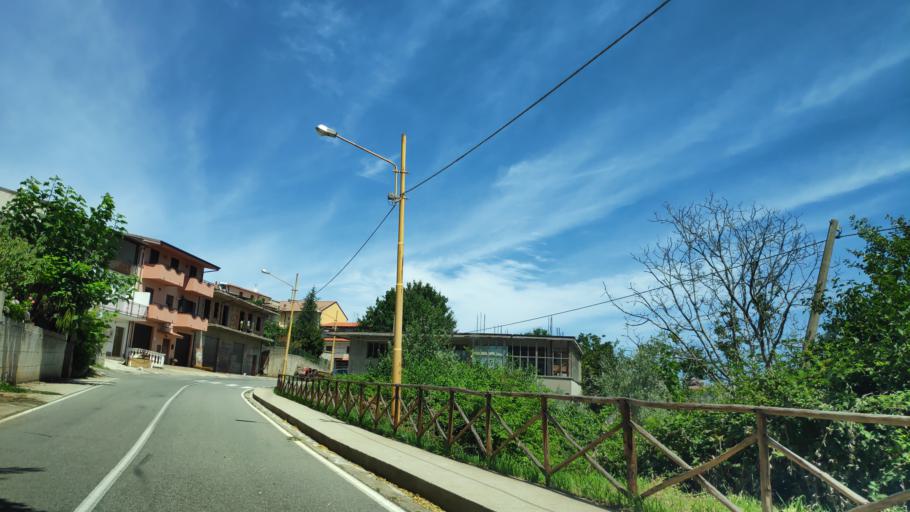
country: IT
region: Calabria
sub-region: Provincia di Catanzaro
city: Palermiti
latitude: 38.7460
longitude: 16.4507
